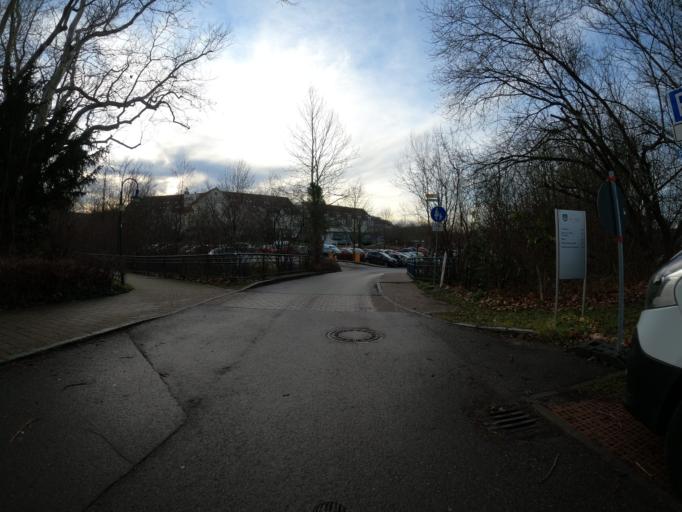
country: DE
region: Baden-Wuerttemberg
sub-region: Regierungsbezirk Stuttgart
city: Boll
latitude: 48.6394
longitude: 9.5983
